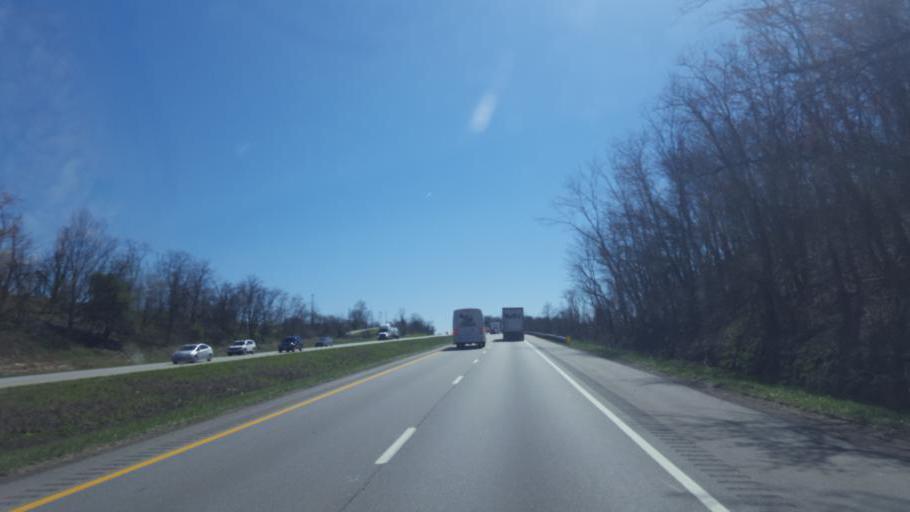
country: US
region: Ohio
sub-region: Belmont County
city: Barnesville
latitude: 40.0581
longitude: -81.2976
